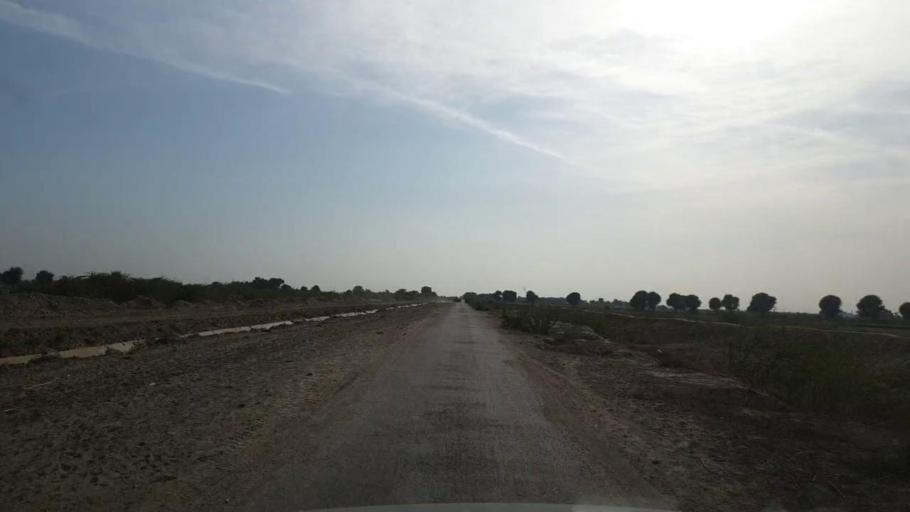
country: PK
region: Sindh
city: Kunri
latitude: 25.1565
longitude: 69.5128
